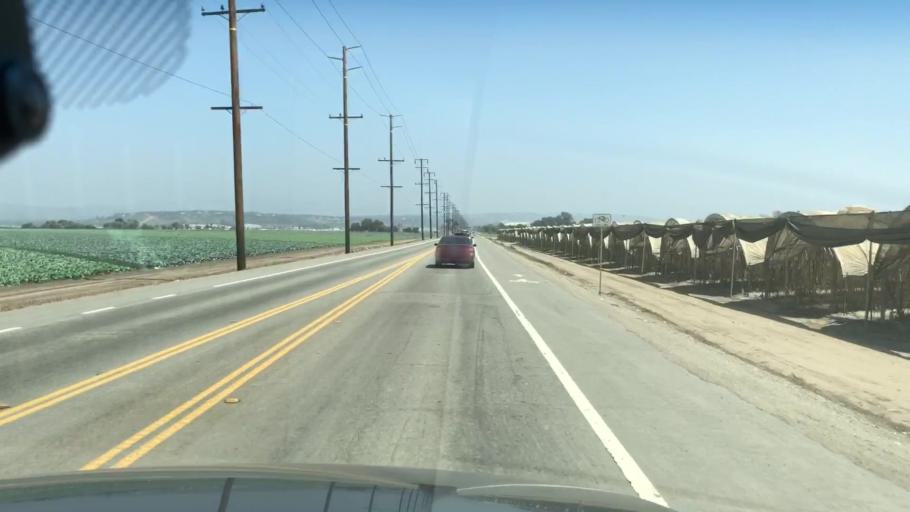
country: US
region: California
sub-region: Ventura County
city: Oxnard
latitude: 34.1867
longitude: -119.1137
